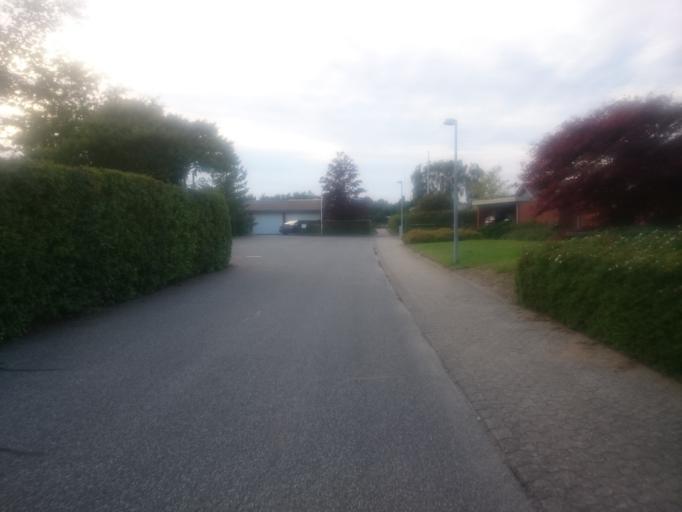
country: DK
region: South Denmark
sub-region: Billund Kommune
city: Billund
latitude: 55.7246
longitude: 9.0981
